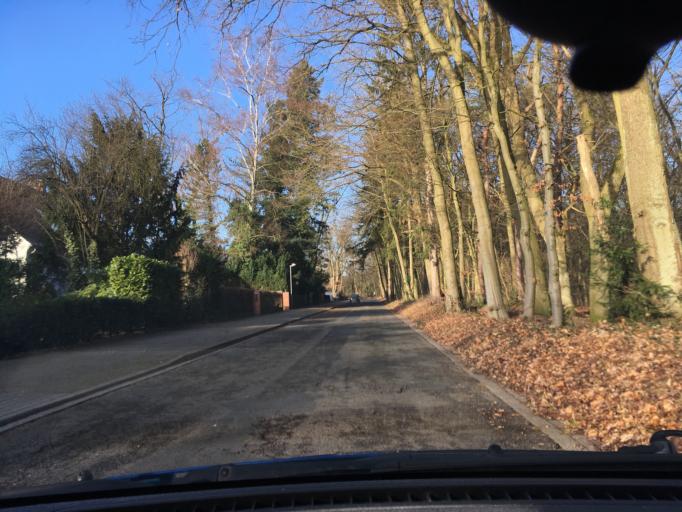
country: DE
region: Lower Saxony
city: Lueneburg
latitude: 53.2243
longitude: 10.4093
